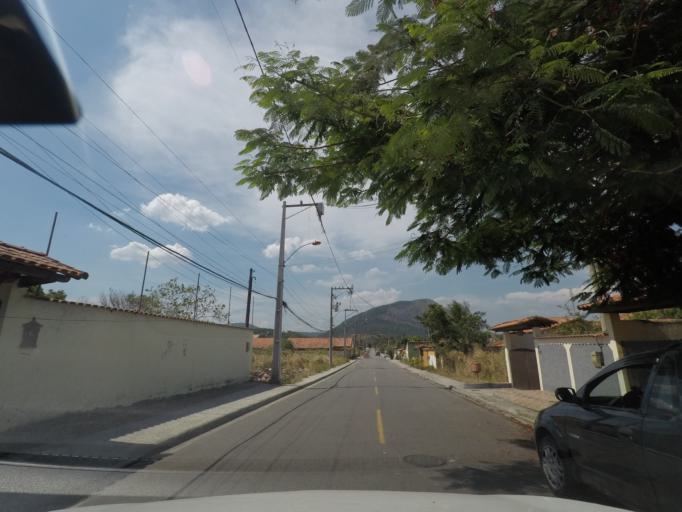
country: BR
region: Rio de Janeiro
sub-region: Marica
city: Marica
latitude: -22.9636
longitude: -42.9657
